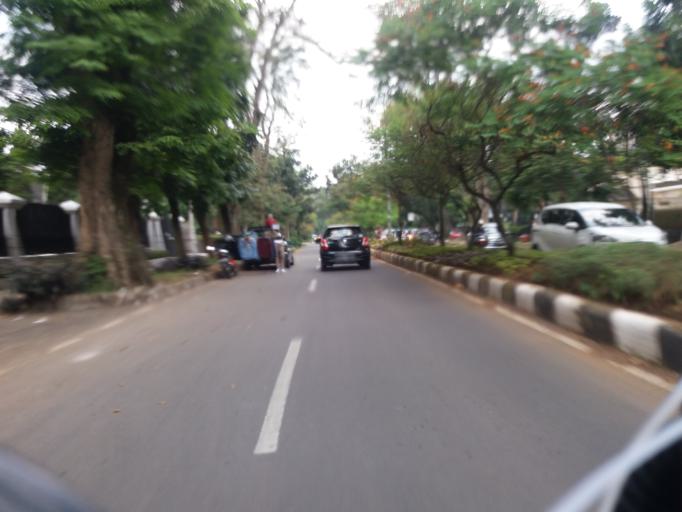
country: ID
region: West Java
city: Bandung
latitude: -6.9021
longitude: 107.6246
